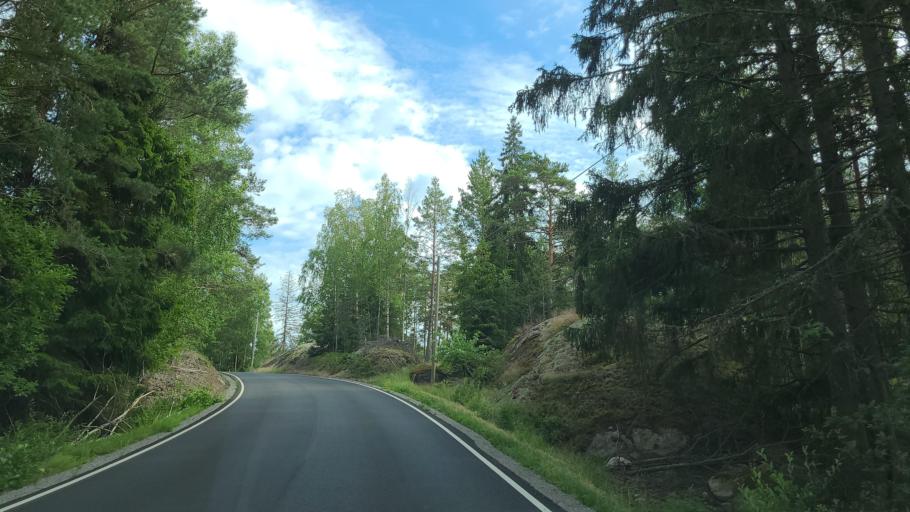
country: FI
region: Varsinais-Suomi
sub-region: Turku
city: Rymaettylae
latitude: 60.3210
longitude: 21.9568
